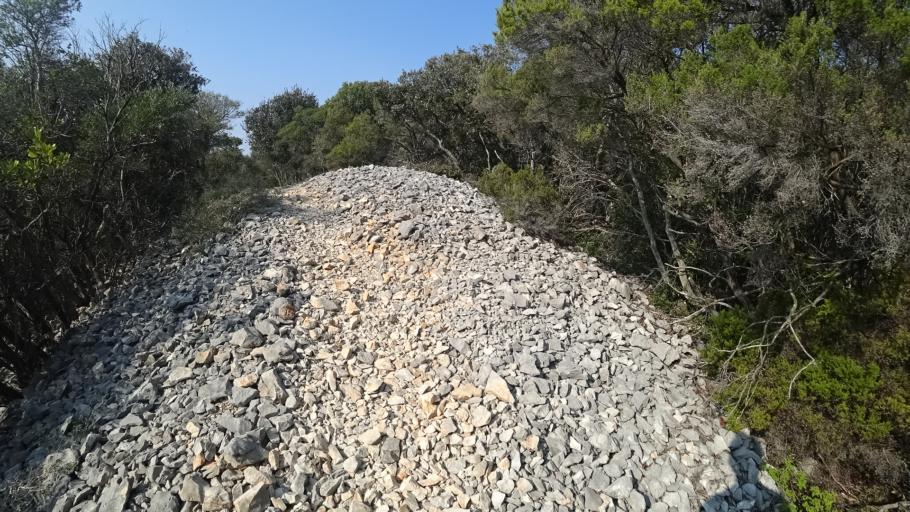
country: HR
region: Primorsko-Goranska
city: Mali Losinj
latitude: 44.4842
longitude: 14.5101
